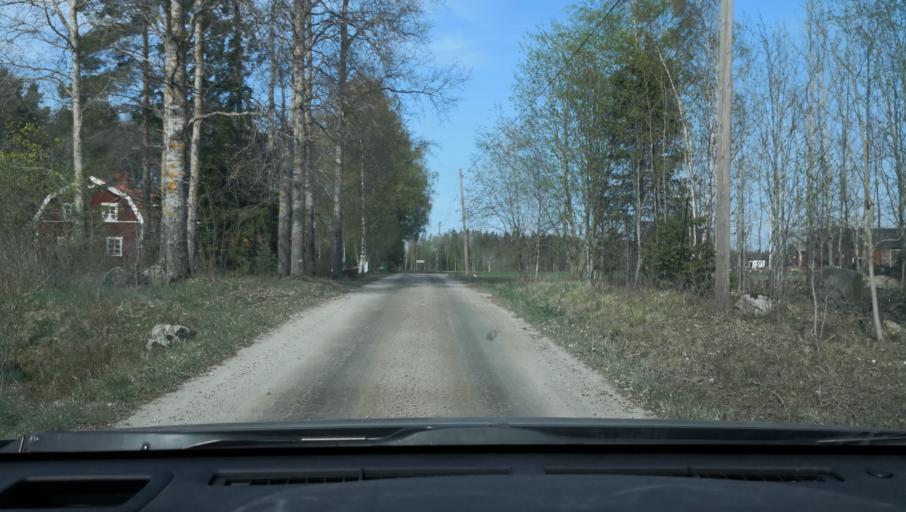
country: SE
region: Vaestmanland
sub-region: Vasteras
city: Skultuna
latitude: 59.8032
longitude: 16.4342
